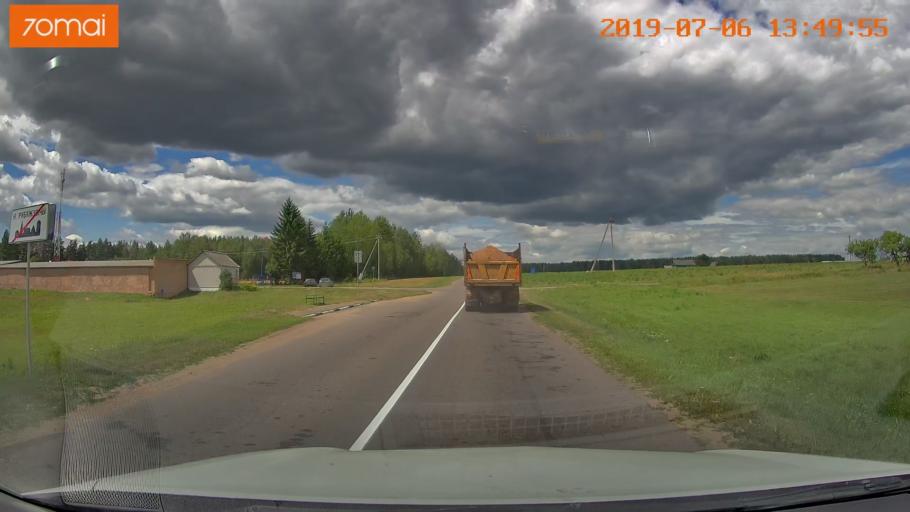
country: BY
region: Minsk
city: Ivyanyets
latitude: 53.6961
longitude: 26.8487
